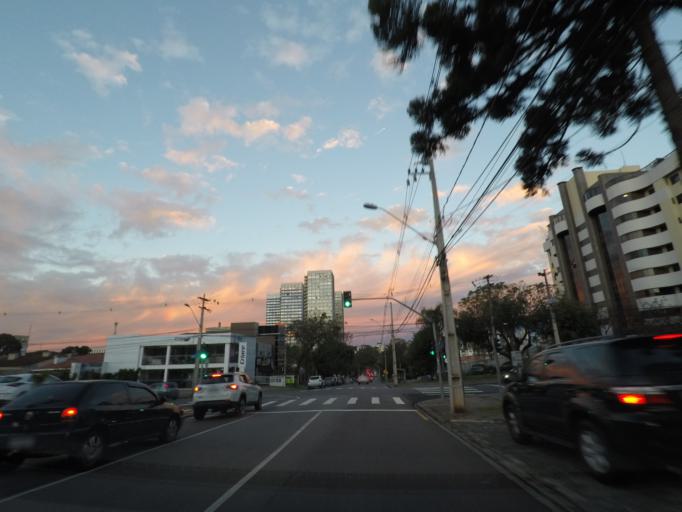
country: BR
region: Parana
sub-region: Curitiba
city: Curitiba
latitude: -25.4308
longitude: -49.2544
